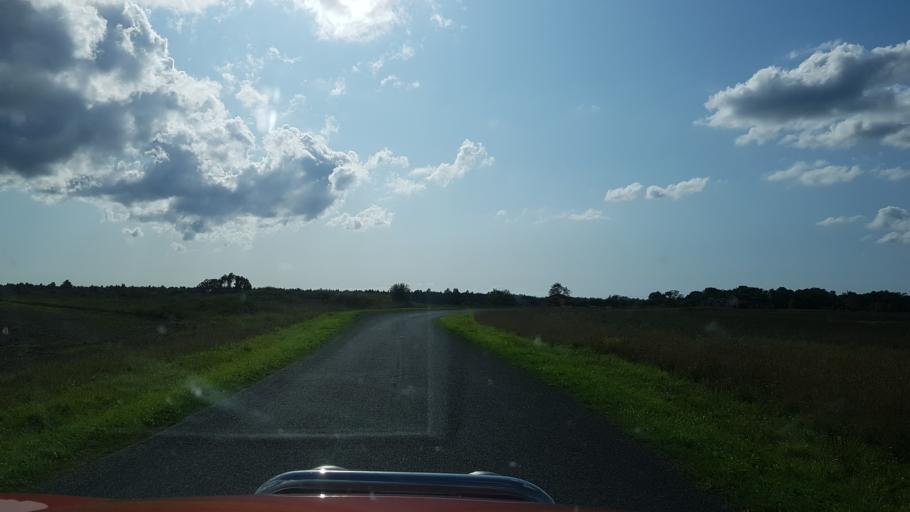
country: EE
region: Harju
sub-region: Paldiski linn
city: Paldiski
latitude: 59.1992
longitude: 23.9503
